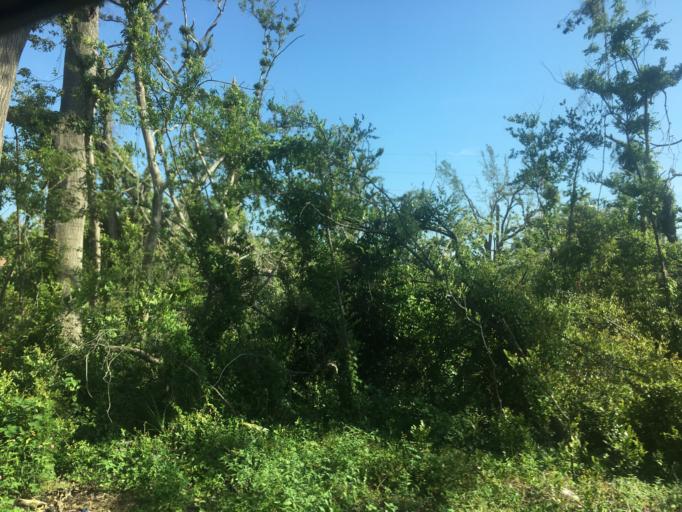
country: US
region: Florida
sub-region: Bay County
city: Springfield
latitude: 30.1466
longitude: -85.6187
